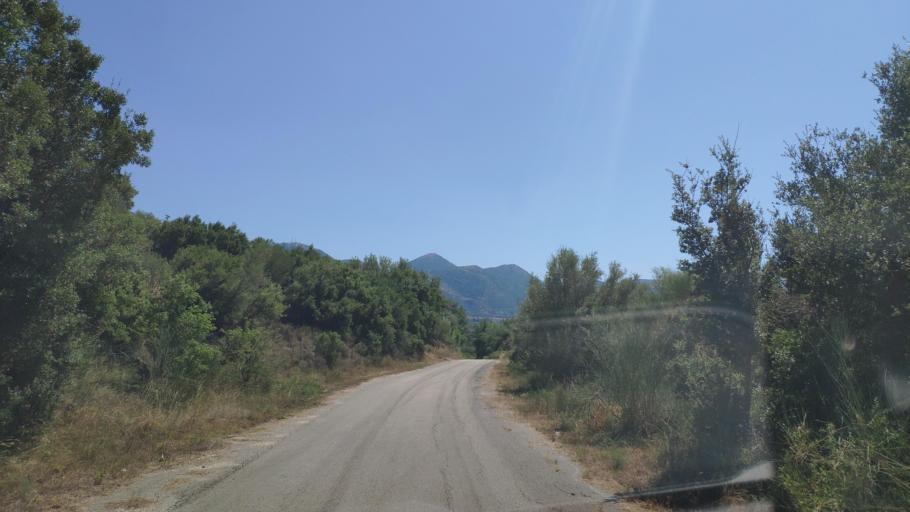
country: GR
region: Epirus
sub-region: Nomos Prevezis
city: Kanalaki
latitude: 39.2724
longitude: 20.6001
